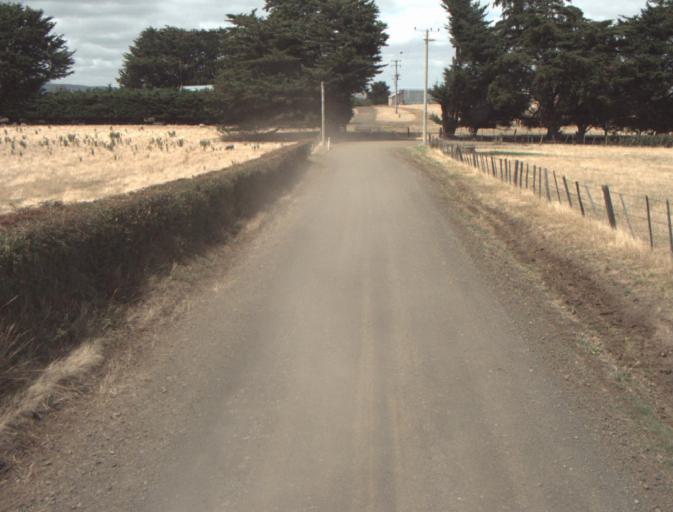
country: AU
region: Tasmania
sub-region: Northern Midlands
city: Evandale
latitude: -41.5225
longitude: 147.2836
